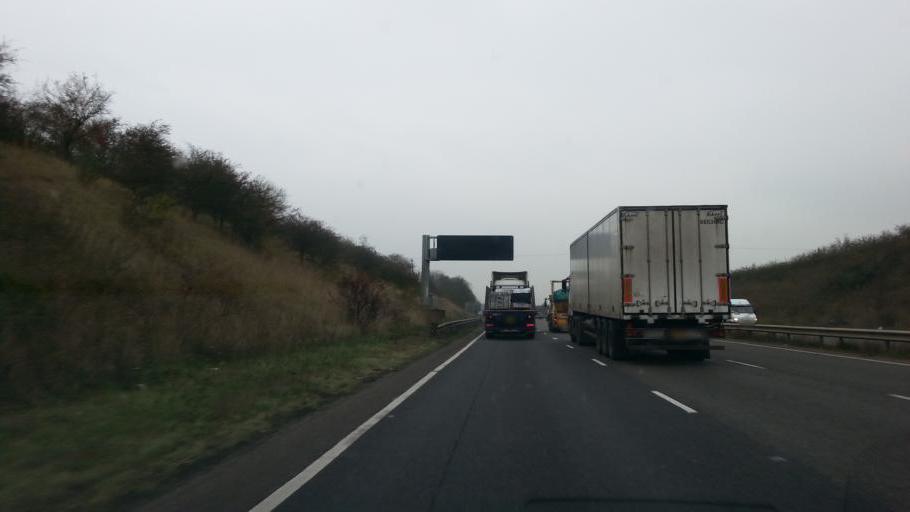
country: GB
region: England
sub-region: Suffolk
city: Exning
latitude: 52.2361
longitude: 0.3326
